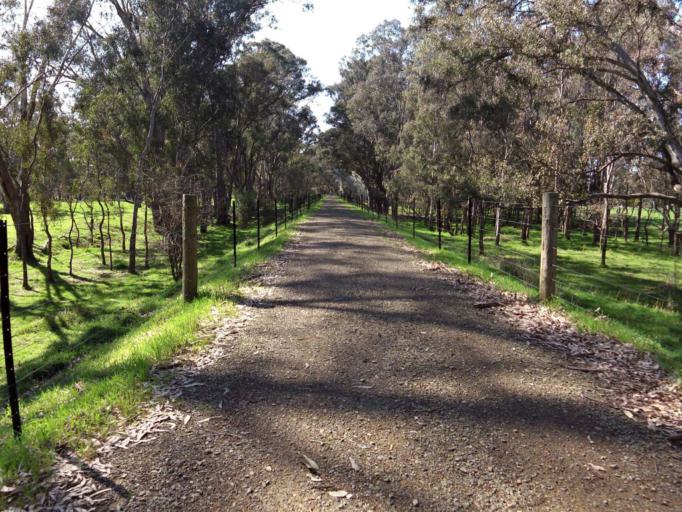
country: AU
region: Victoria
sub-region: Murrindindi
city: Alexandra
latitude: -37.1620
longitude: 145.5564
